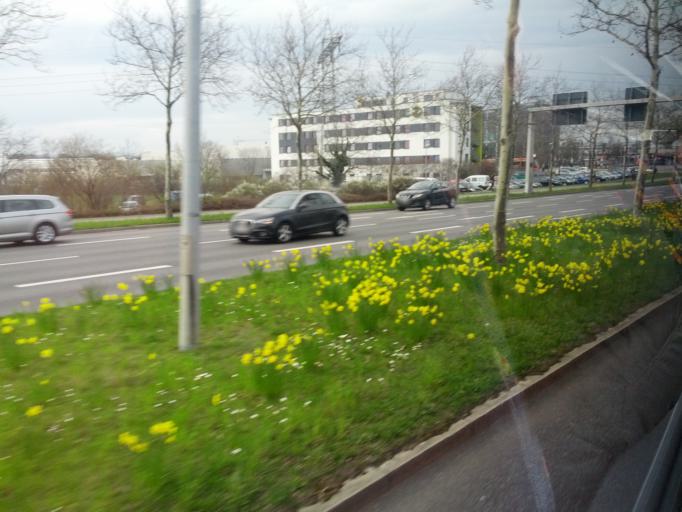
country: DE
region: Baden-Wuerttemberg
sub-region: Freiburg Region
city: Ebringen
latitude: 47.9863
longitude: 7.7964
